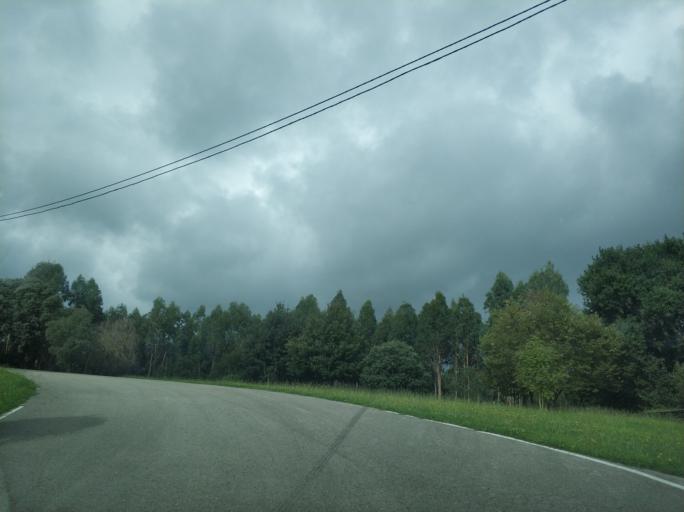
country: ES
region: Cantabria
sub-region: Provincia de Cantabria
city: San Miguel de Meruelo
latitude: 43.4339
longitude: -3.5787
